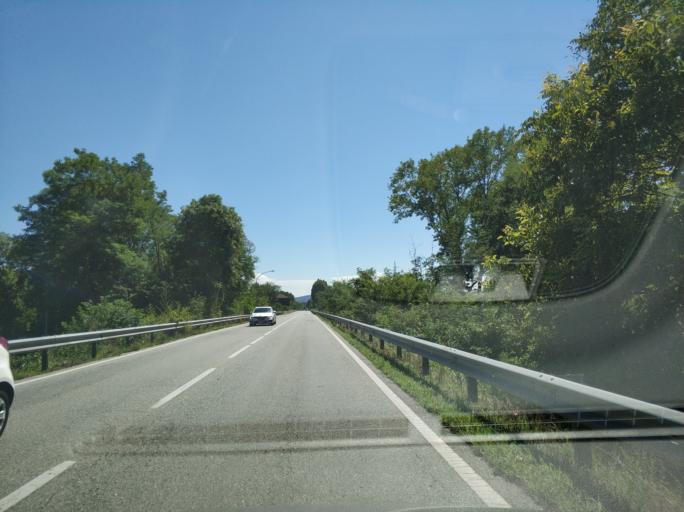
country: IT
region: Piedmont
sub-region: Provincia di Torino
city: Rondissone
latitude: 45.2662
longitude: 7.9771
